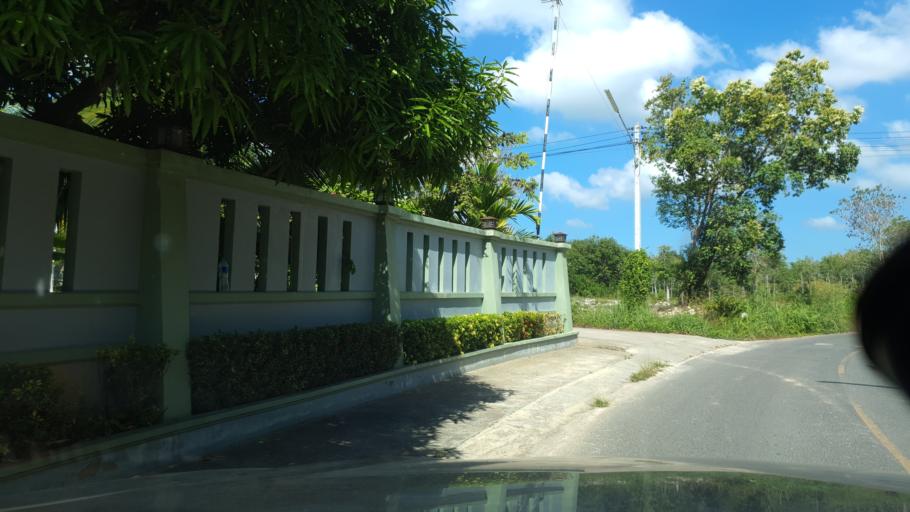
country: TH
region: Phangnga
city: Ban Ao Nang
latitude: 8.0318
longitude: 98.8568
